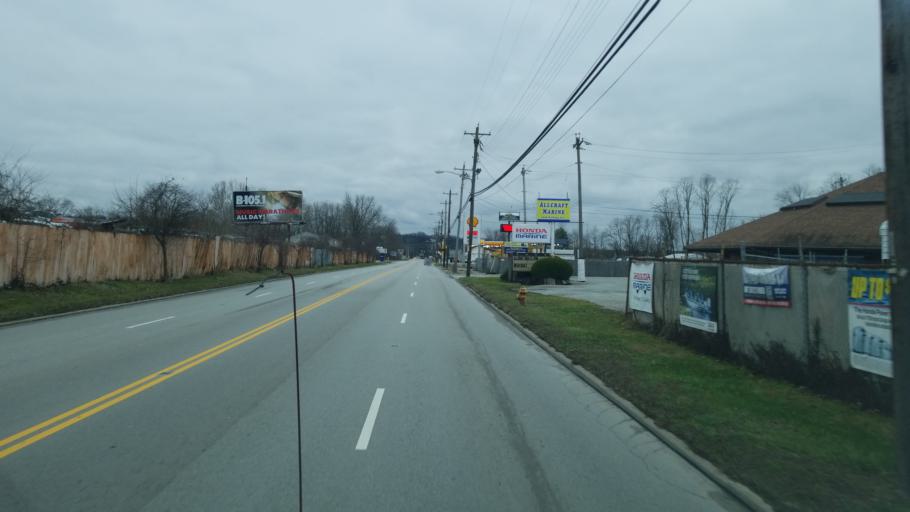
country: US
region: Kentucky
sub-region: Campbell County
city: Fort Thomas
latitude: 39.0976
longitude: -84.4304
